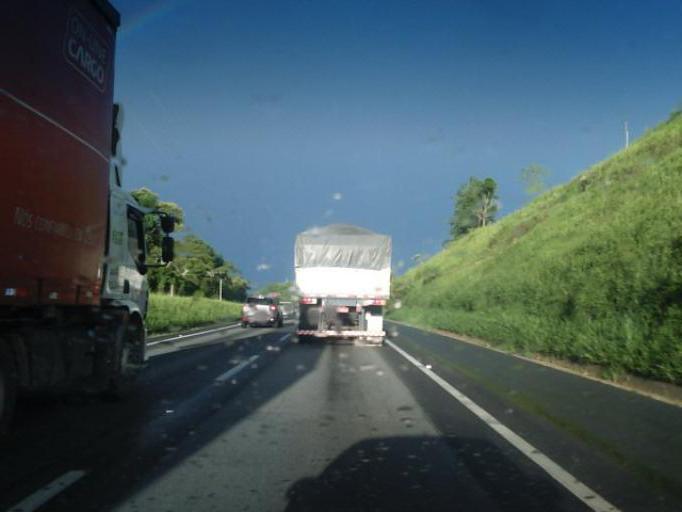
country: BR
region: Sao Paulo
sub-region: Juquitiba
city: Juquitiba
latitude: -23.9645
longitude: -47.1256
